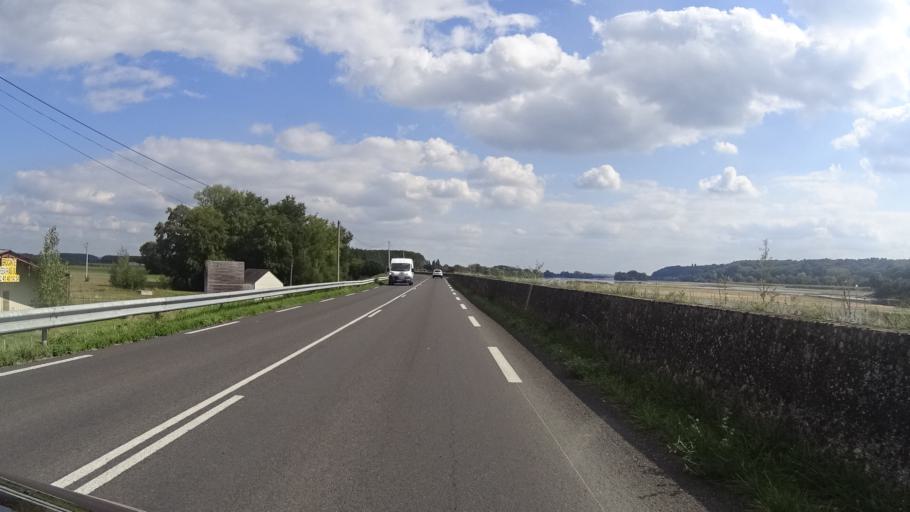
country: FR
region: Pays de la Loire
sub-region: Departement de Maine-et-Loire
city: Saint-Clement-des-Levees
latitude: 47.3253
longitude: -0.1725
